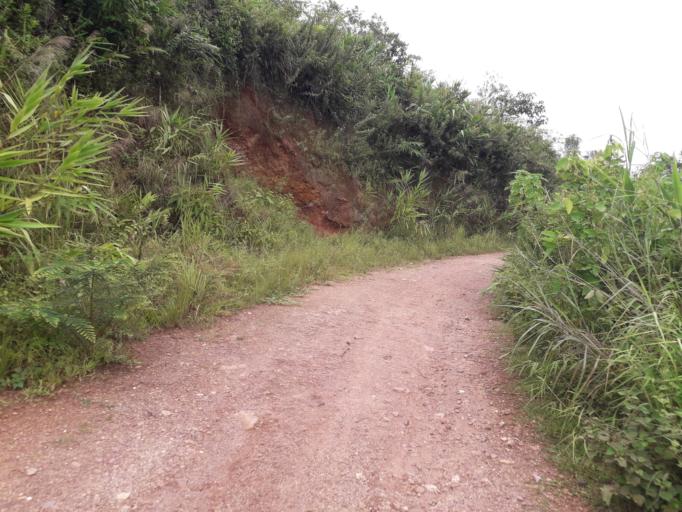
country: CN
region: Yunnan
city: Menglie
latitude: 22.2583
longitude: 101.5964
